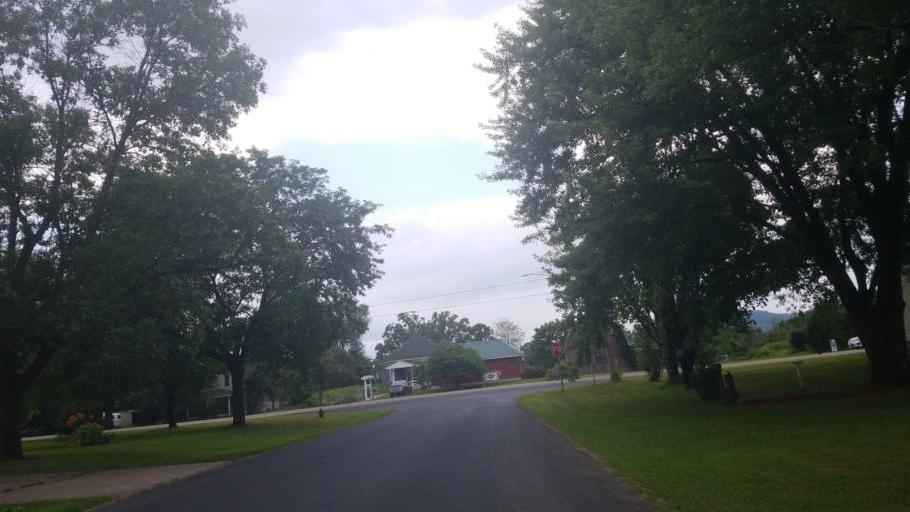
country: US
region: Wisconsin
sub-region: Dunn County
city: Menomonie
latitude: 44.7751
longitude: -91.9279
